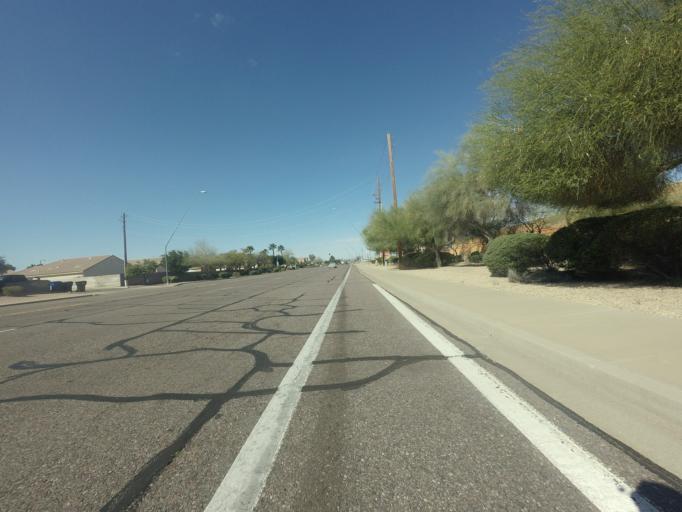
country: US
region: Arizona
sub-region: Maricopa County
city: Mesa
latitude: 33.4664
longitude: -111.7031
